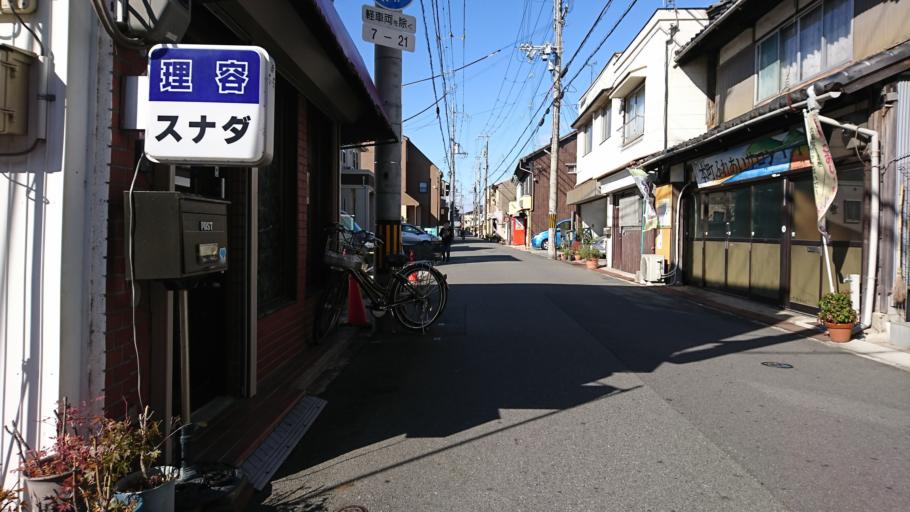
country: JP
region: Hyogo
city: Kakogawacho-honmachi
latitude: 34.7691
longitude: 134.8338
